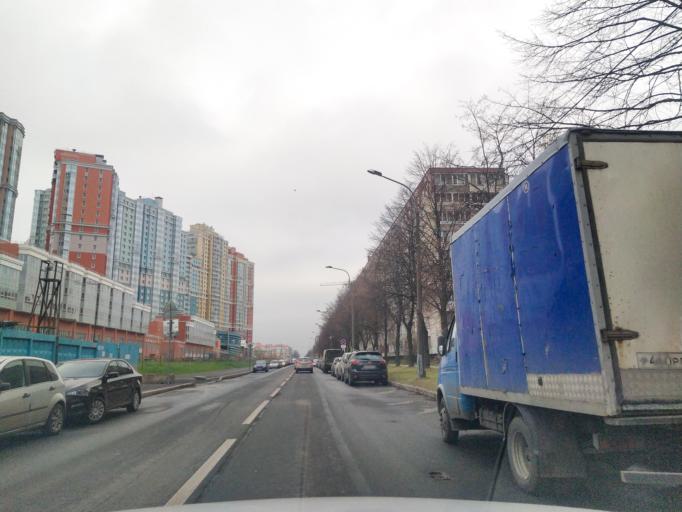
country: RU
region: St.-Petersburg
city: Sosnovka
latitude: 60.0421
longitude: 30.3629
